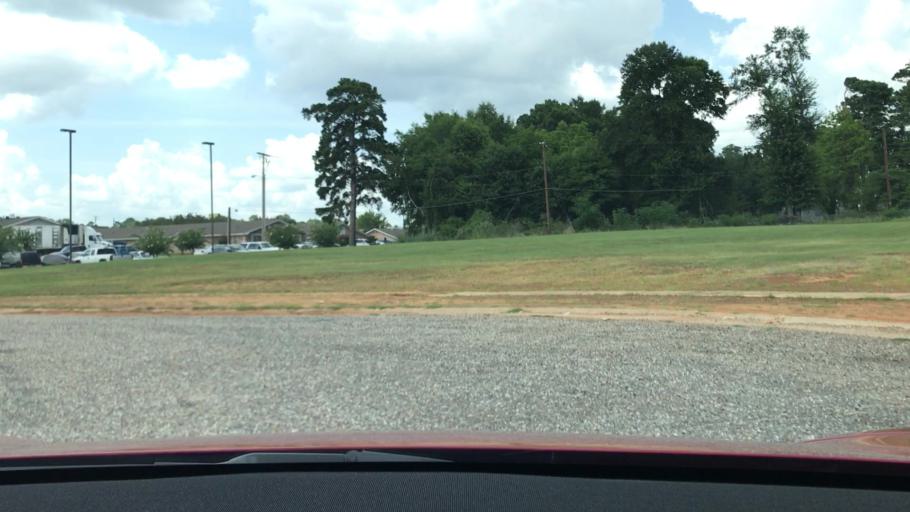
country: US
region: Louisiana
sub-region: De Soto Parish
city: Stonewall
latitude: 32.3976
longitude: -93.8041
